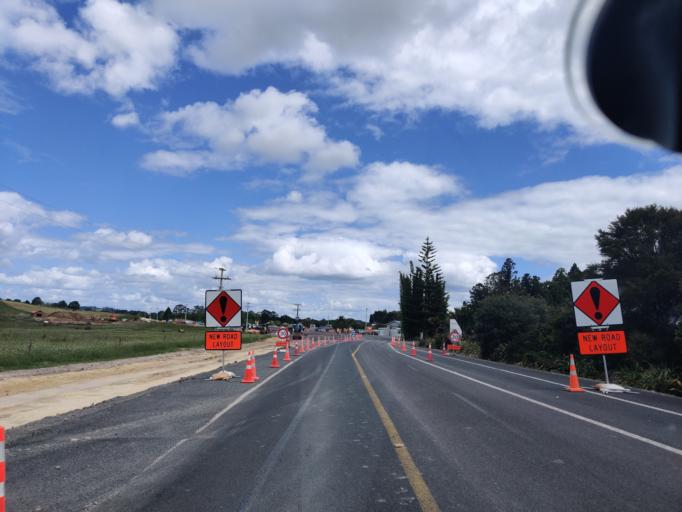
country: NZ
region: Northland
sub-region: Far North District
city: Kerikeri
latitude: -35.3010
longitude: 173.9621
